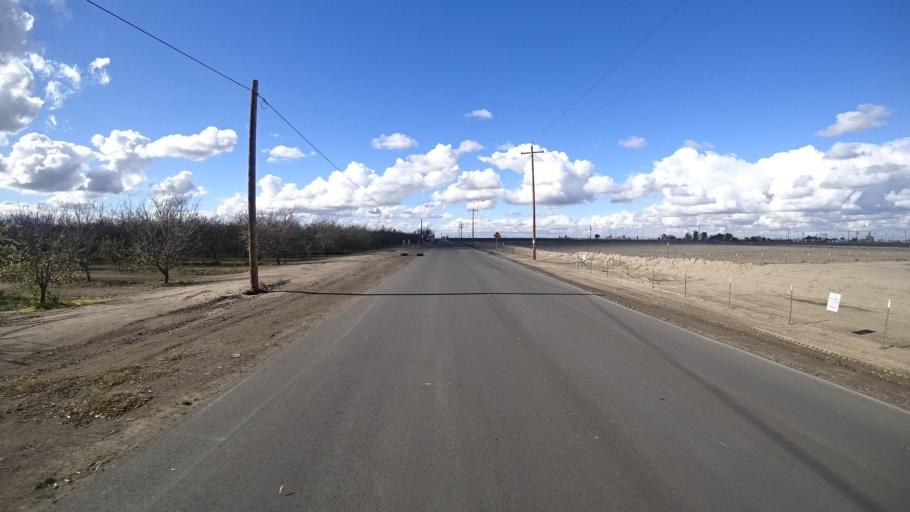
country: US
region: California
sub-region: Kern County
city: Greenfield
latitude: 35.2602
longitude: -119.0726
